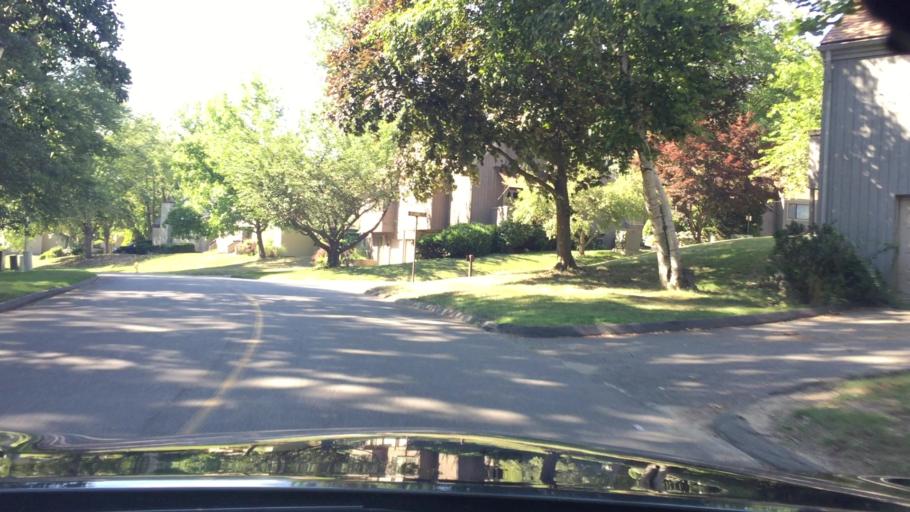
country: US
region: Connecticut
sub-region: New Haven County
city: City of Milford (balance)
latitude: 41.2467
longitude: -73.1079
